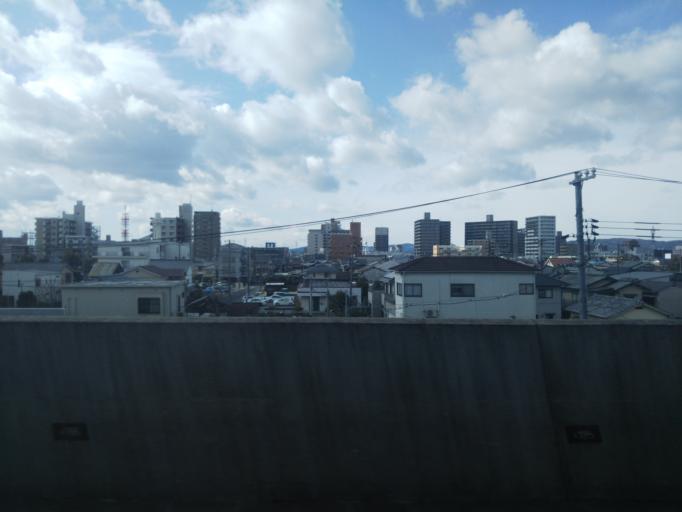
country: JP
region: Okayama
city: Okayama-shi
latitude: 34.6416
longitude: 133.9099
